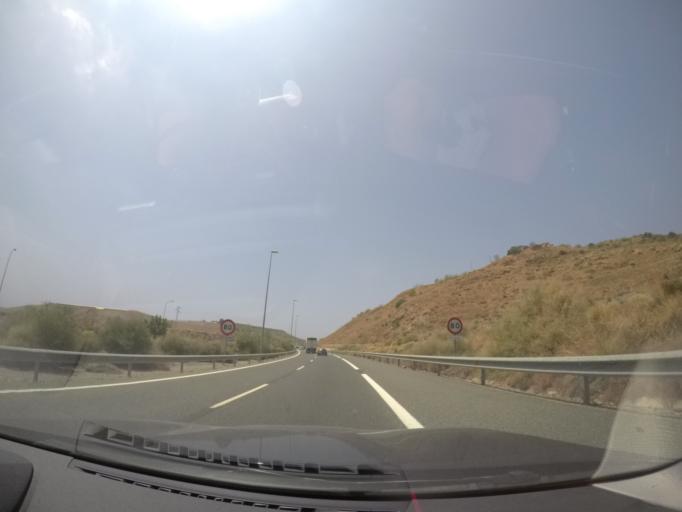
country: ES
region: Andalusia
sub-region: Provincia de Granada
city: Polopos
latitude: 36.7487
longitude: -3.3296
